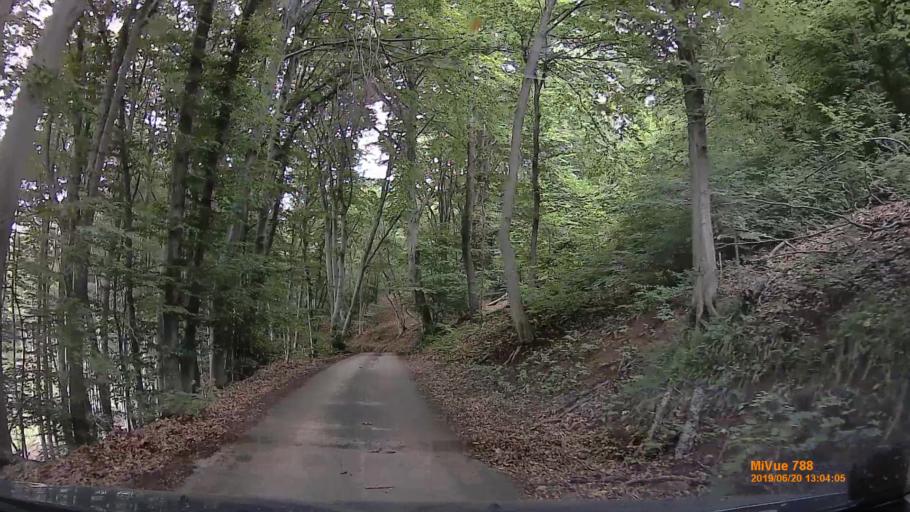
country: HU
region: Baranya
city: Hosszuheteny
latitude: 46.2131
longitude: 18.3619
